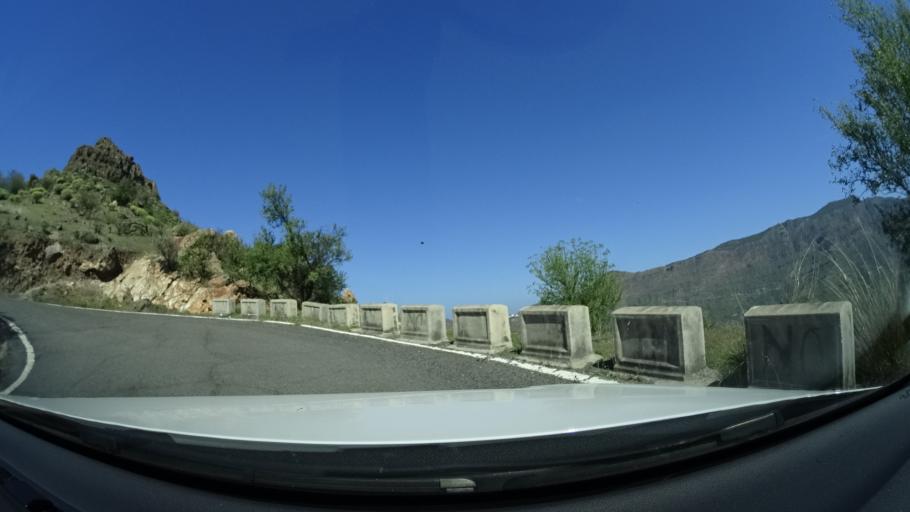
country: ES
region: Canary Islands
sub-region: Provincia de Las Palmas
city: Tejeda
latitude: 27.9900
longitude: -15.6374
